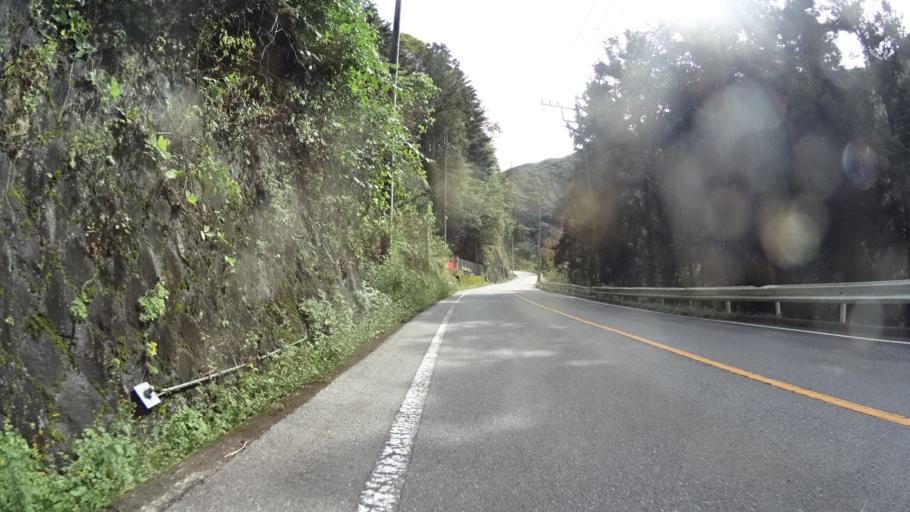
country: JP
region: Yamanashi
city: Otsuki
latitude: 35.7875
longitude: 138.9456
